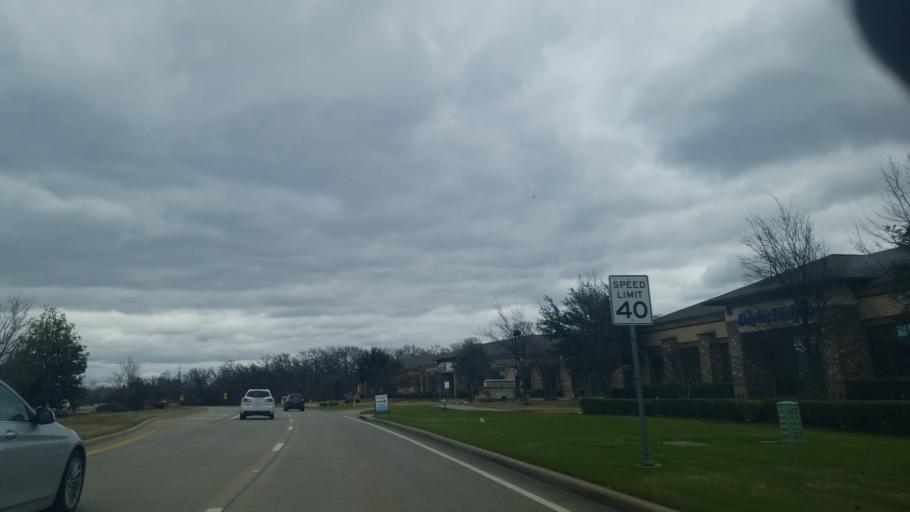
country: US
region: Texas
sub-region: Denton County
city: Copper Canyon
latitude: 33.0783
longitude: -97.0795
